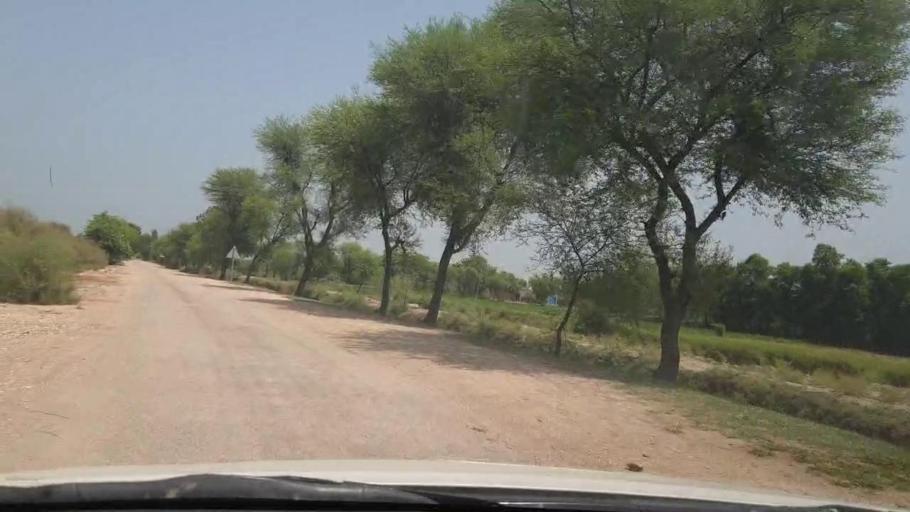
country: PK
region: Sindh
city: Rustam jo Goth
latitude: 28.0272
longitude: 68.7607
